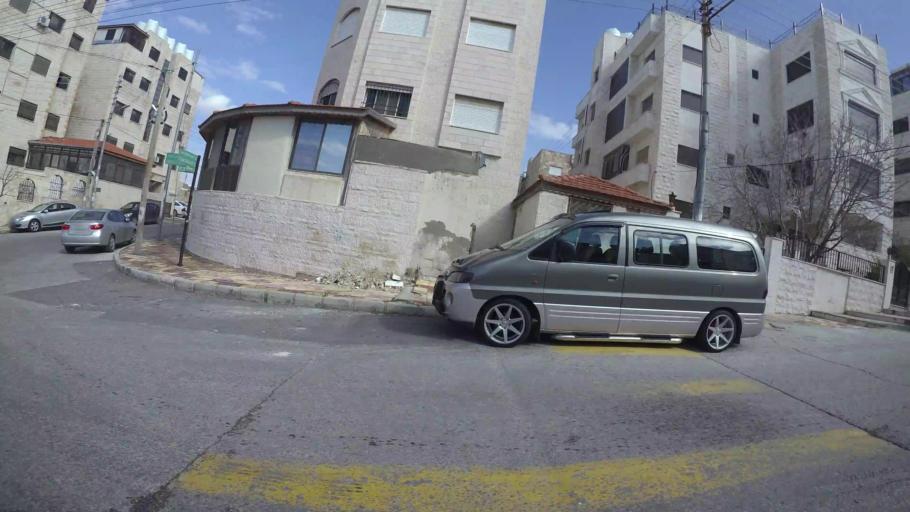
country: JO
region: Amman
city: Al Jubayhah
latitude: 32.0238
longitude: 35.8545
